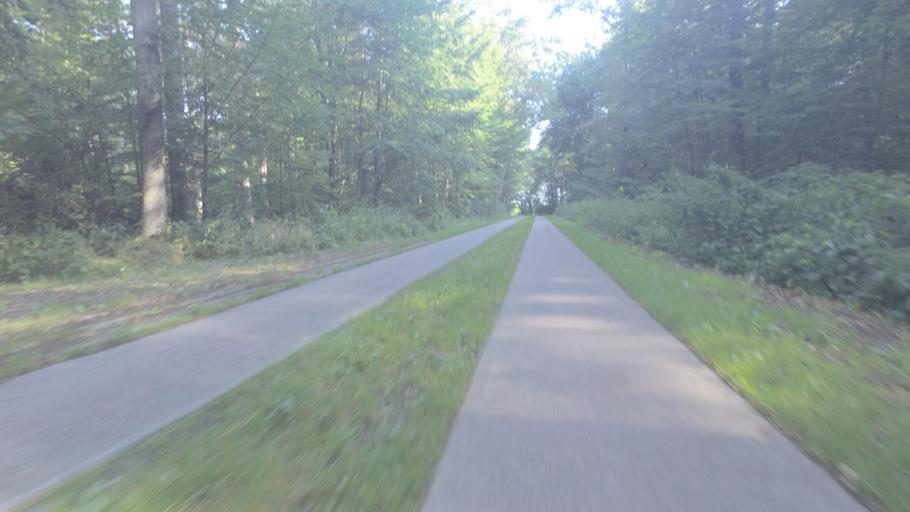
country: DE
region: Mecklenburg-Vorpommern
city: Wittenhagen
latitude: 54.1721
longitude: 13.0727
